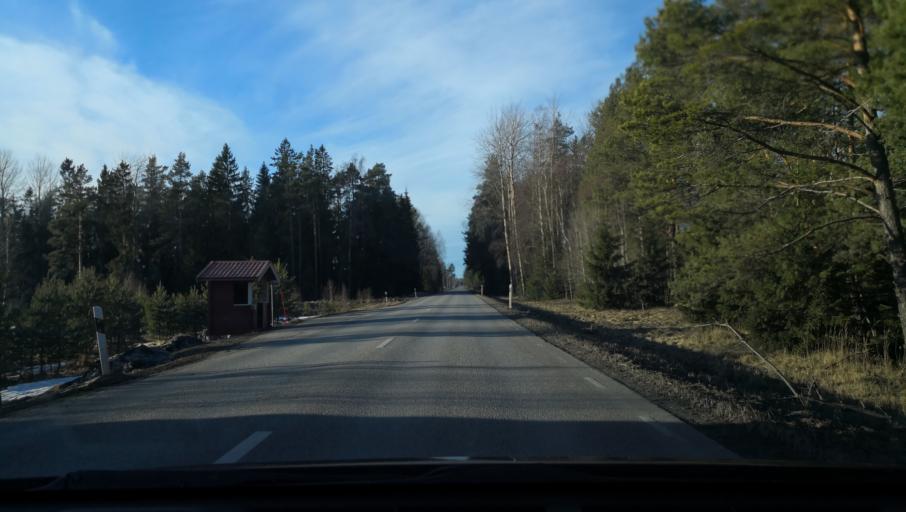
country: SE
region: Uppsala
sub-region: Osthammars Kommun
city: OEsthammar
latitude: 60.2767
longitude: 18.3032
